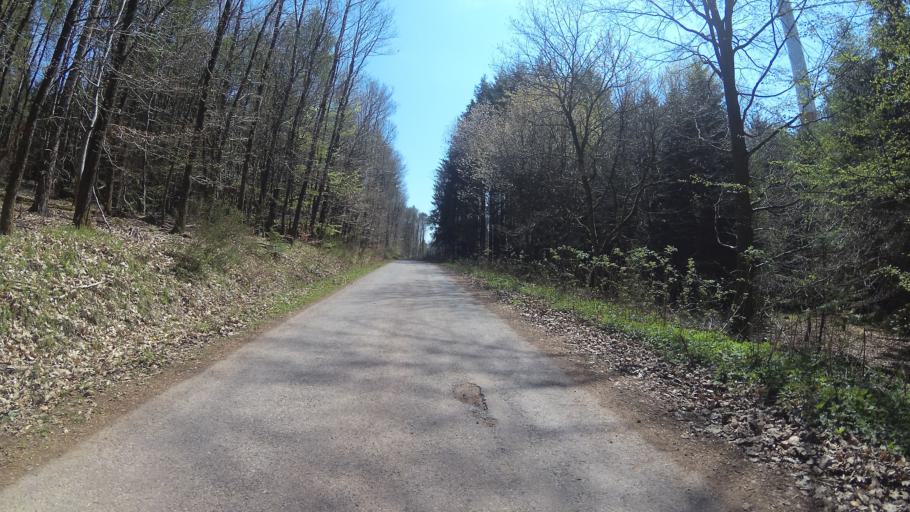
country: DE
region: Rheinland-Pfalz
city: Dunzweiler
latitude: 49.4072
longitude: 7.2891
